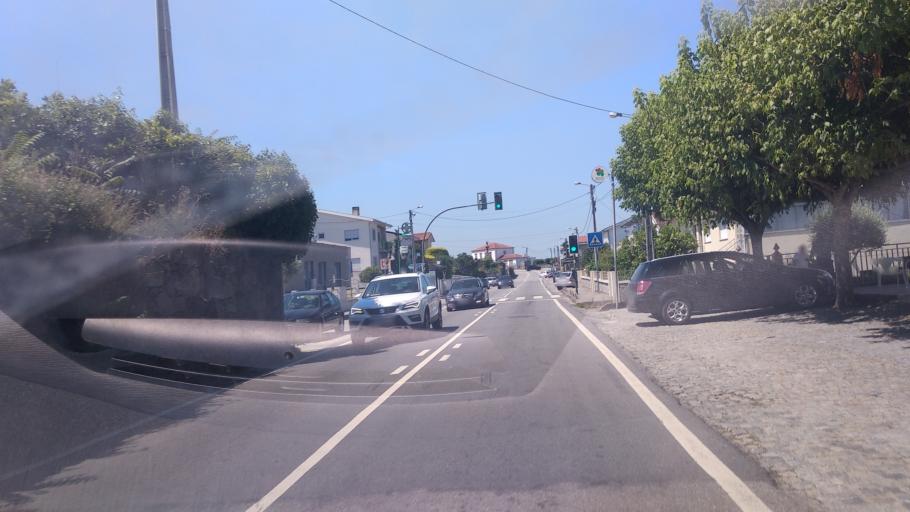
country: PT
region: Braga
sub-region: Braga
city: Adaufe
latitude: 41.5865
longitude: -8.4017
